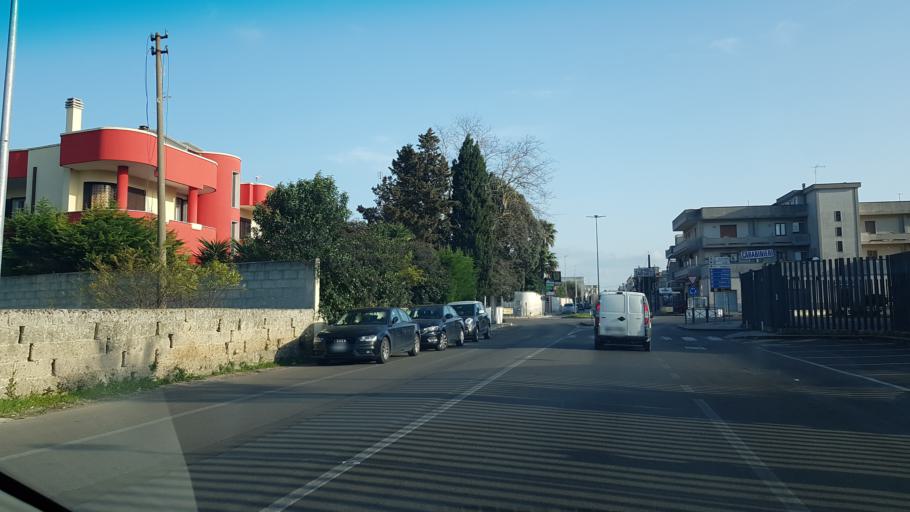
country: IT
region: Apulia
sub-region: Provincia di Lecce
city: Trepuzzi
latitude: 40.4104
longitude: 18.0667
